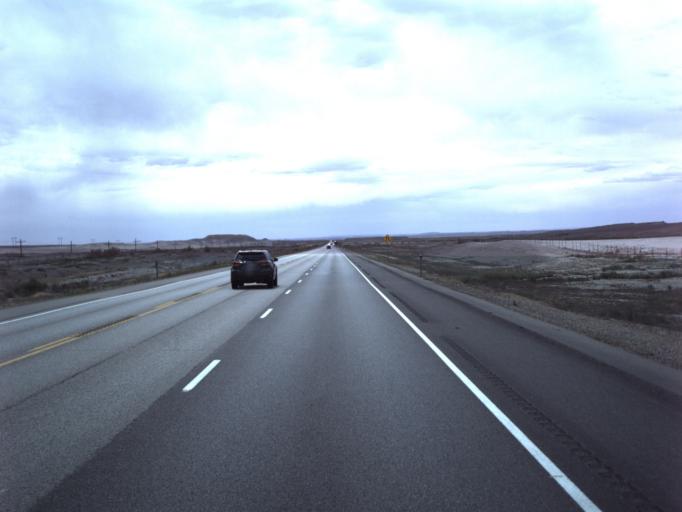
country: US
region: Utah
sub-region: Carbon County
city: East Carbon City
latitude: 39.1093
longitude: -110.3265
